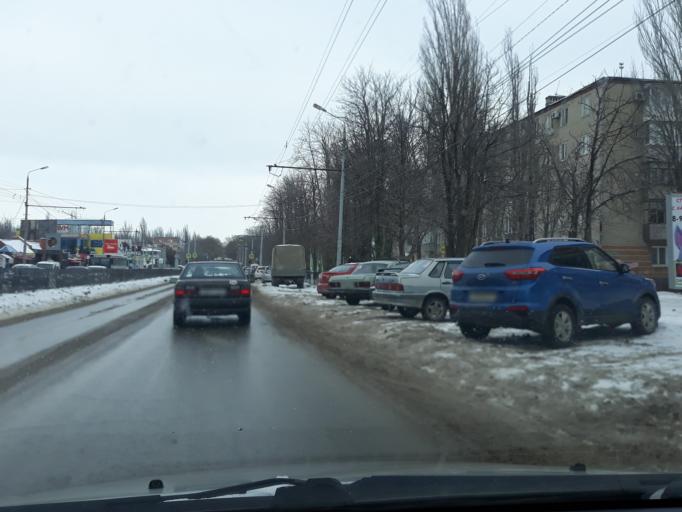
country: RU
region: Rostov
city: Taganrog
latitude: 47.2503
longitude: 38.9179
